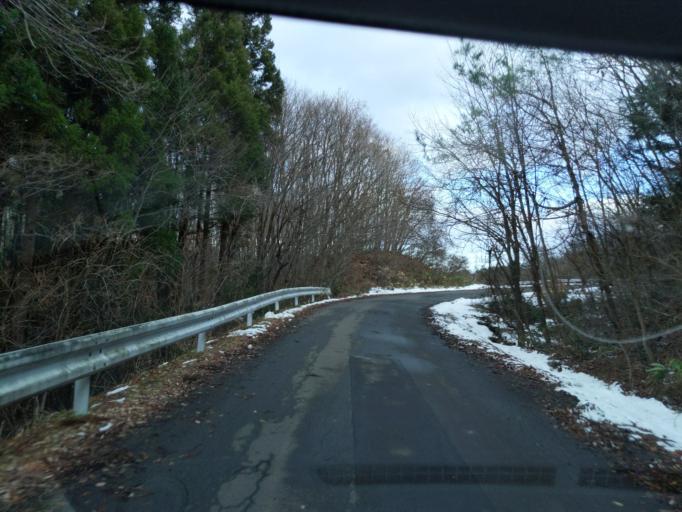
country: JP
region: Iwate
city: Ichinoseki
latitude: 38.9934
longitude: 140.9993
